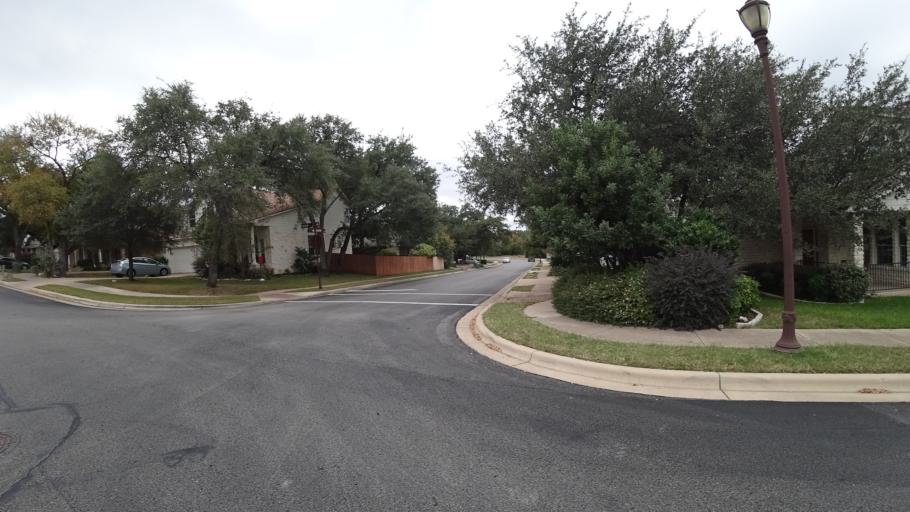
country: US
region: Texas
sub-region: Williamson County
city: Brushy Creek
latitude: 30.5094
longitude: -97.7477
